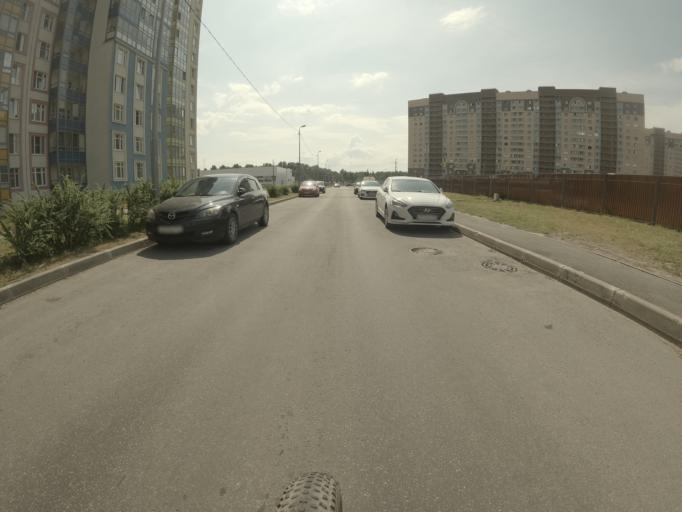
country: RU
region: St.-Petersburg
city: Krasnogvargeisky
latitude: 59.9159
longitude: 30.4378
